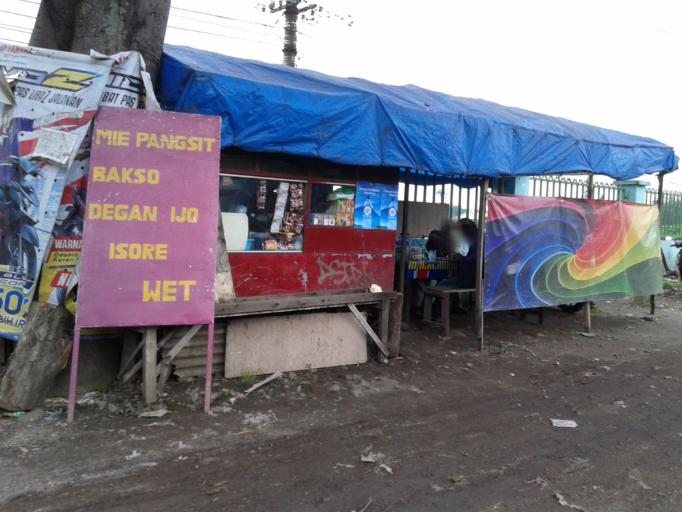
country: ID
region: East Java
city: Singosari
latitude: -7.8657
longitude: 112.6836
